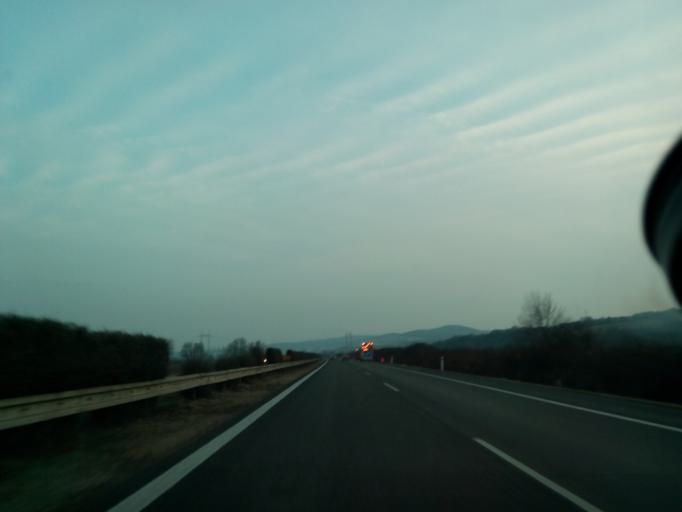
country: SK
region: Presovsky
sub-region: Okres Presov
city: Presov
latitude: 48.8920
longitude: 21.2487
